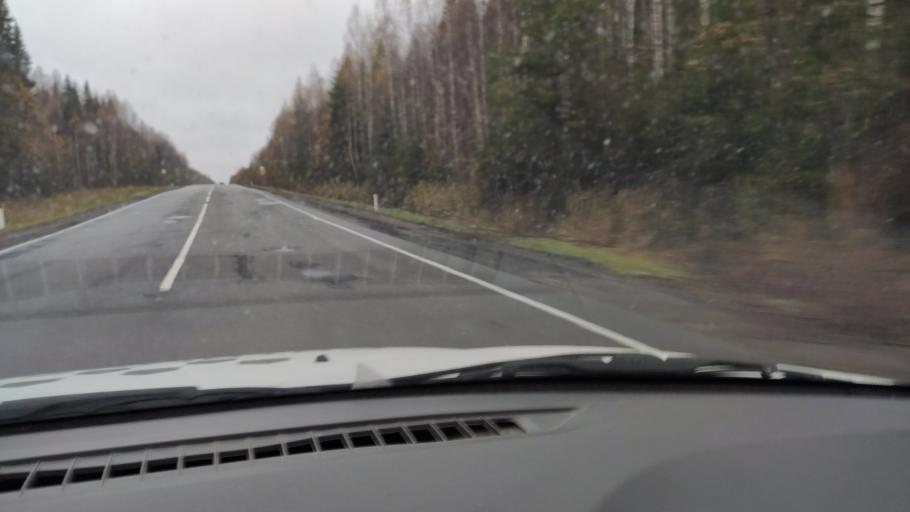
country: RU
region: Kirov
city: Omutninsk
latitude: 58.7611
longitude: 52.0077
